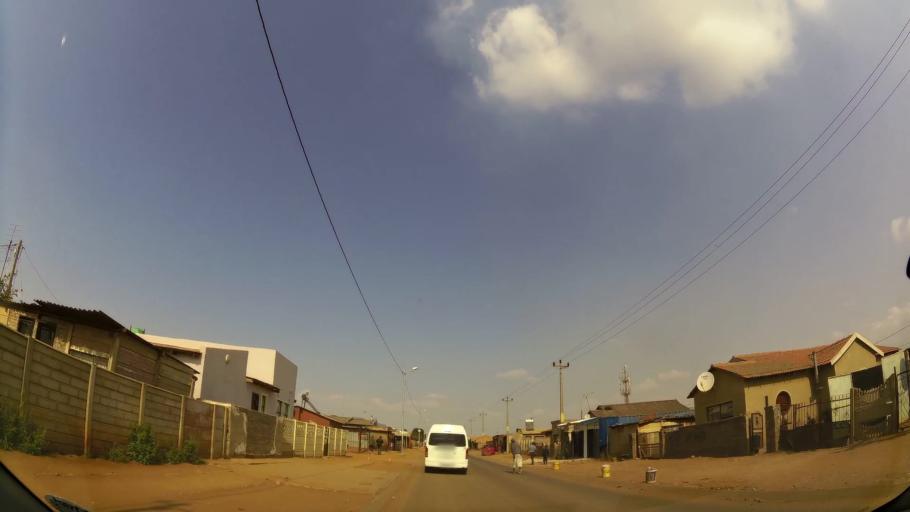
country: ZA
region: Gauteng
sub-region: Ekurhuleni Metropolitan Municipality
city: Springs
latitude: -26.1132
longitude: 28.4852
